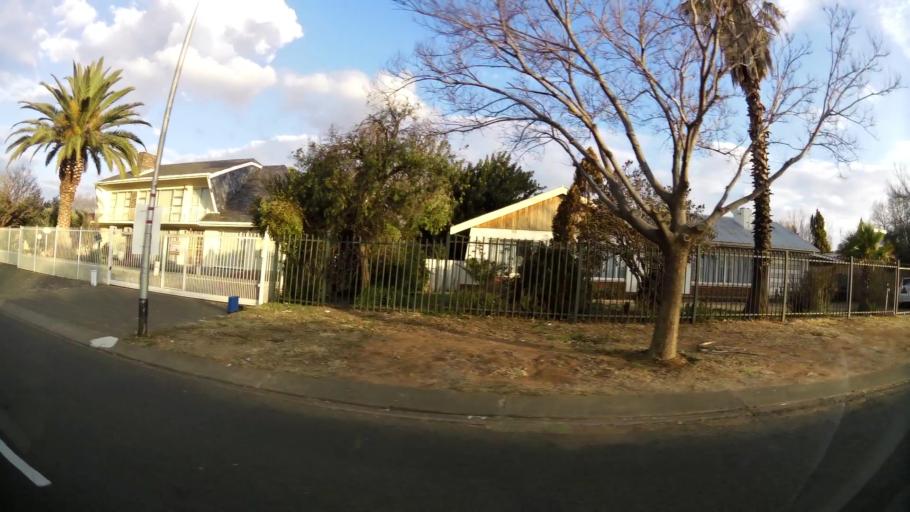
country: ZA
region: Orange Free State
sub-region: Mangaung Metropolitan Municipality
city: Bloemfontein
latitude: -29.1377
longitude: 26.1824
